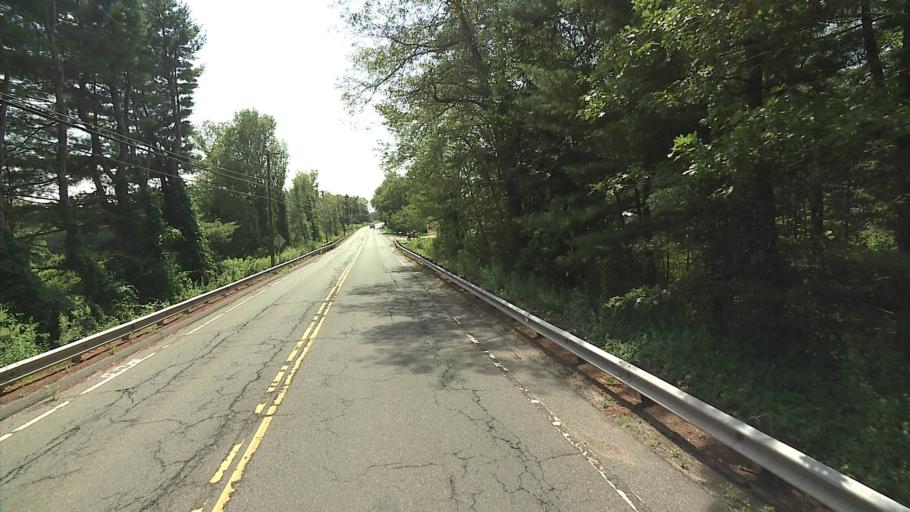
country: US
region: Connecticut
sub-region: Tolland County
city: South Coventry
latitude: 41.7593
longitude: -72.2767
